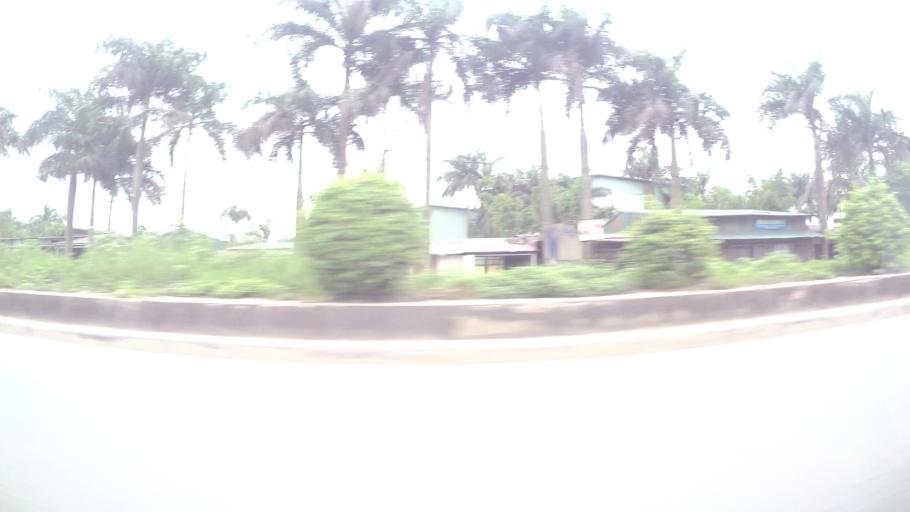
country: VN
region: Ha Noi
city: Hoan Kiem
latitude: 21.0714
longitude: 105.8837
